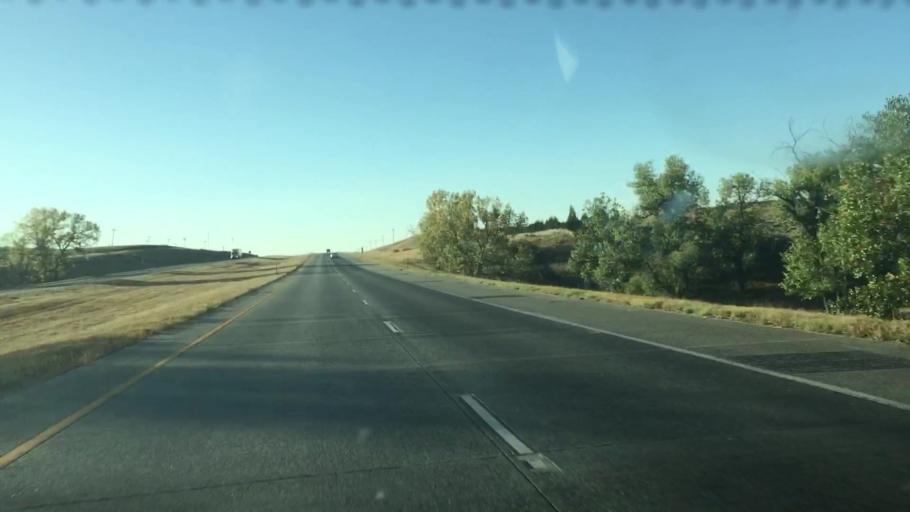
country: US
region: Colorado
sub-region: Arapahoe County
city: Byers
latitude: 39.6729
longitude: -104.1001
